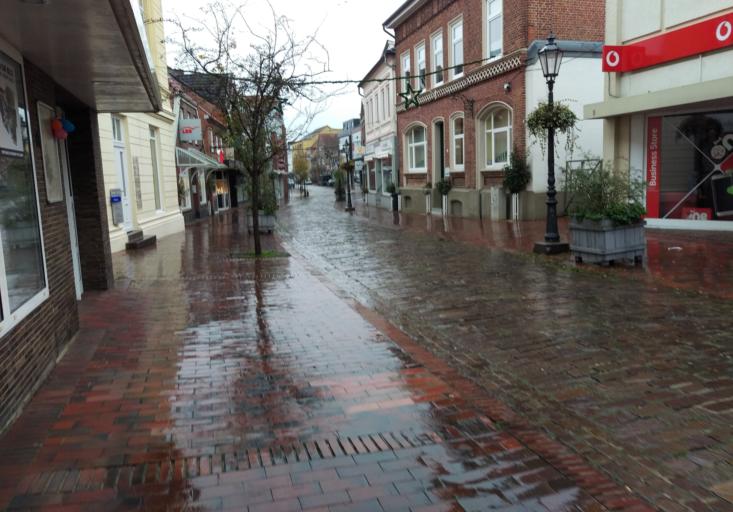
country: DE
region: Schleswig-Holstein
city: Oldenburg in Holstein
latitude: 54.2907
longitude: 10.8860
